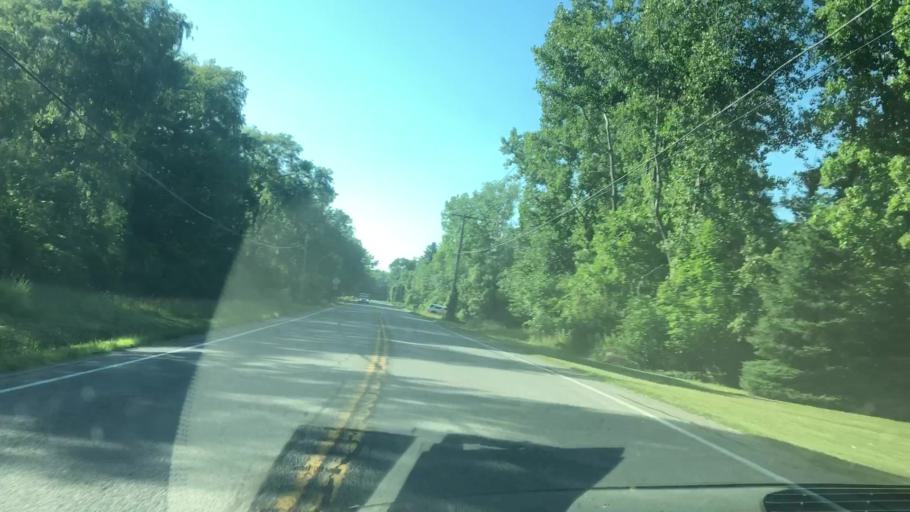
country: US
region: New York
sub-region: Wayne County
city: Ontario
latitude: 43.1805
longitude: -77.2861
